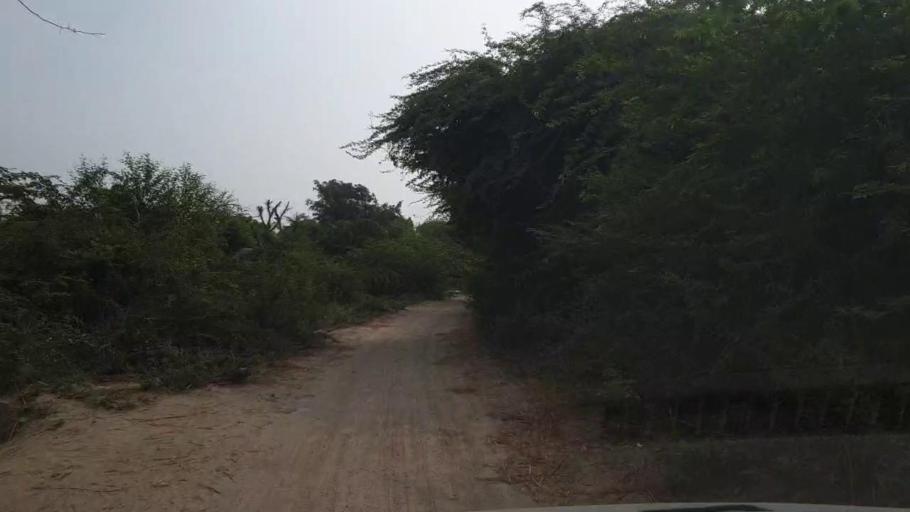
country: PK
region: Sindh
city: Matli
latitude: 24.9786
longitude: 68.7061
